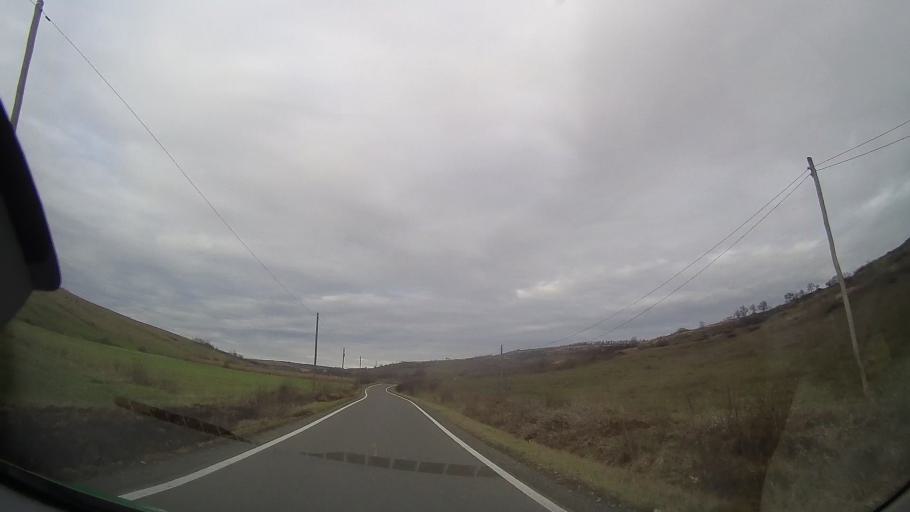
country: RO
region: Mures
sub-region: Comuna Cozma
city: Cozma
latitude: 46.7979
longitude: 24.5390
